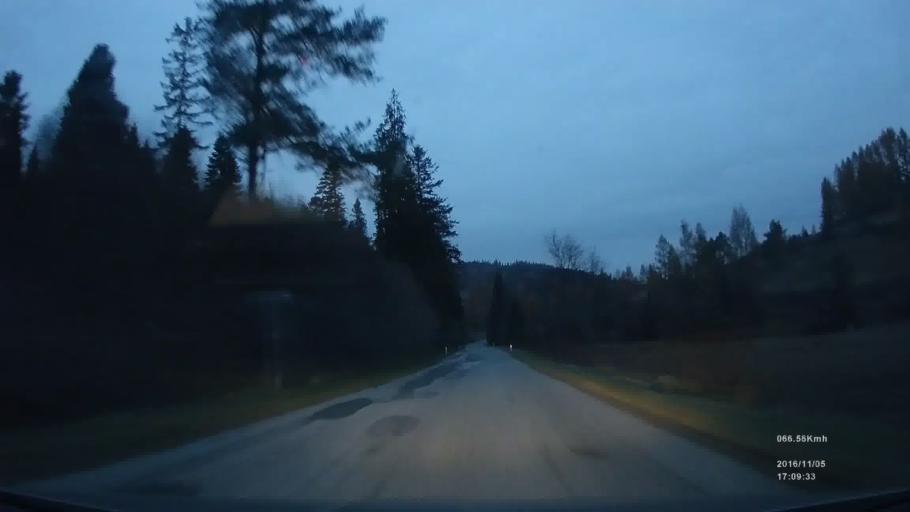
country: SK
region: Presovsky
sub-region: Okres Presov
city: Levoca
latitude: 49.0555
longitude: 20.5145
